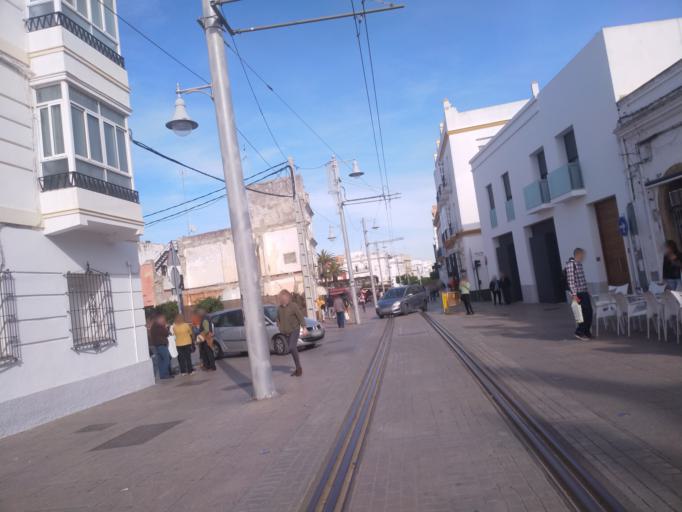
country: ES
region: Andalusia
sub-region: Provincia de Cadiz
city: San Fernando
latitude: 36.4620
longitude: -6.1999
